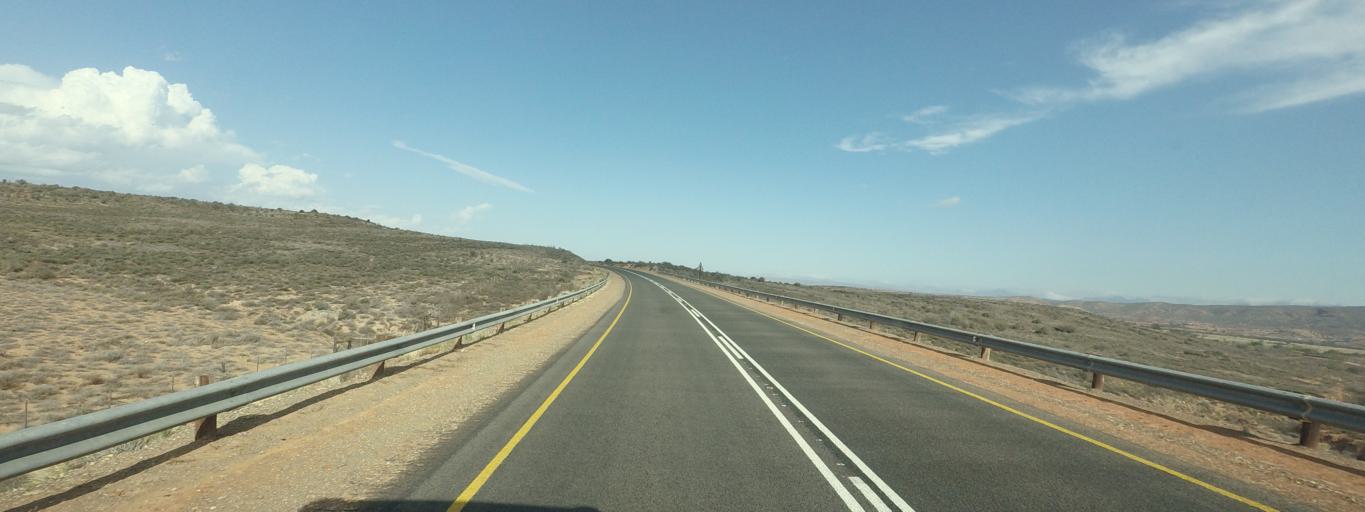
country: ZA
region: Western Cape
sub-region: Eden District Municipality
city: Oudtshoorn
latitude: -33.5961
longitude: 22.0091
